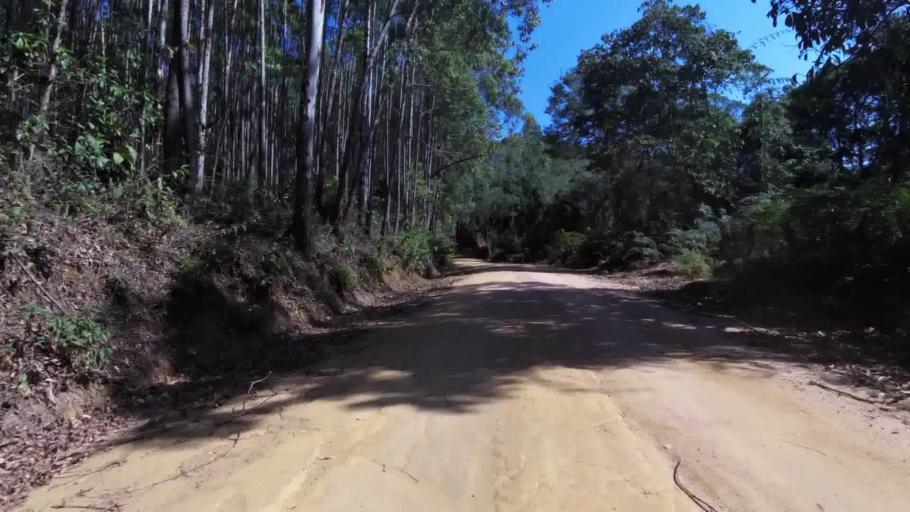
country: BR
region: Espirito Santo
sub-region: Alfredo Chaves
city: Alfredo Chaves
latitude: -20.5196
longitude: -40.8722
